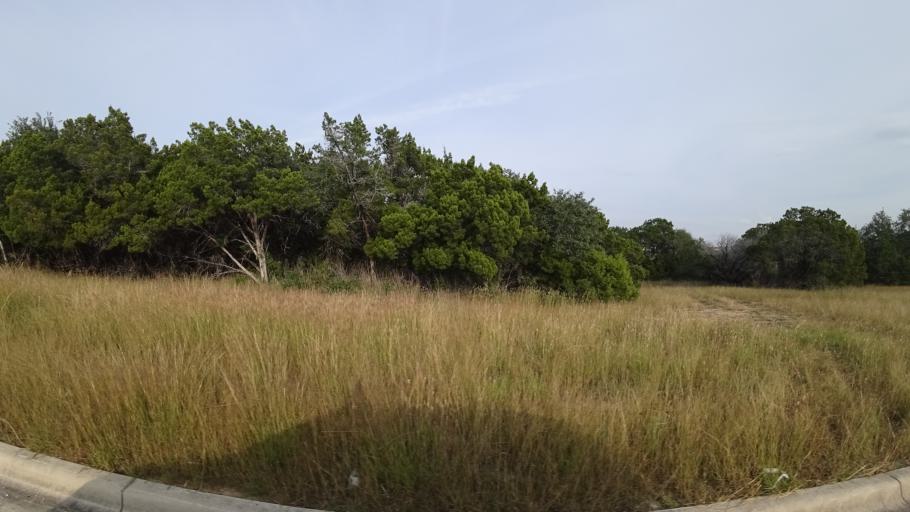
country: US
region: Texas
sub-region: Travis County
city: Hudson Bend
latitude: 30.3859
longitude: -97.8704
